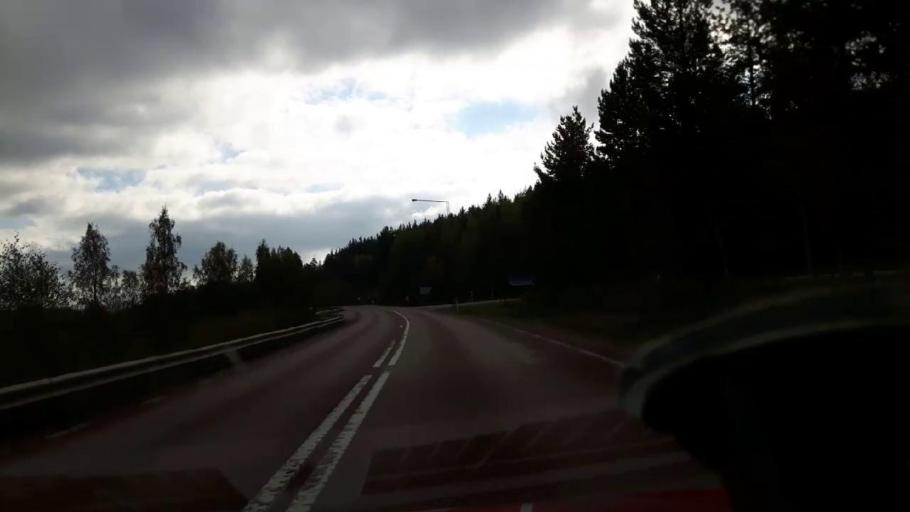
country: SE
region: Gaevleborg
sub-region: Bollnas Kommun
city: Arbra
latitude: 61.5956
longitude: 16.2977
